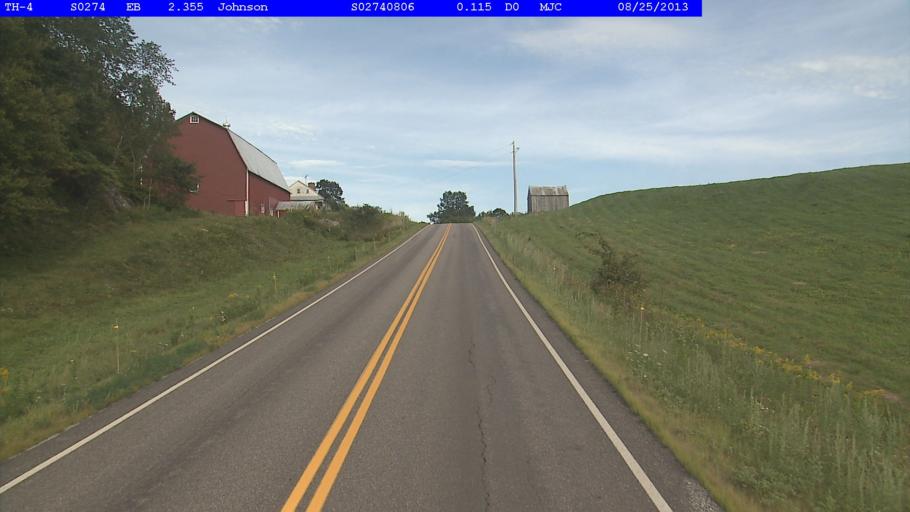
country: US
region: Vermont
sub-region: Lamoille County
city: Johnson
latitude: 44.6559
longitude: -72.7488
